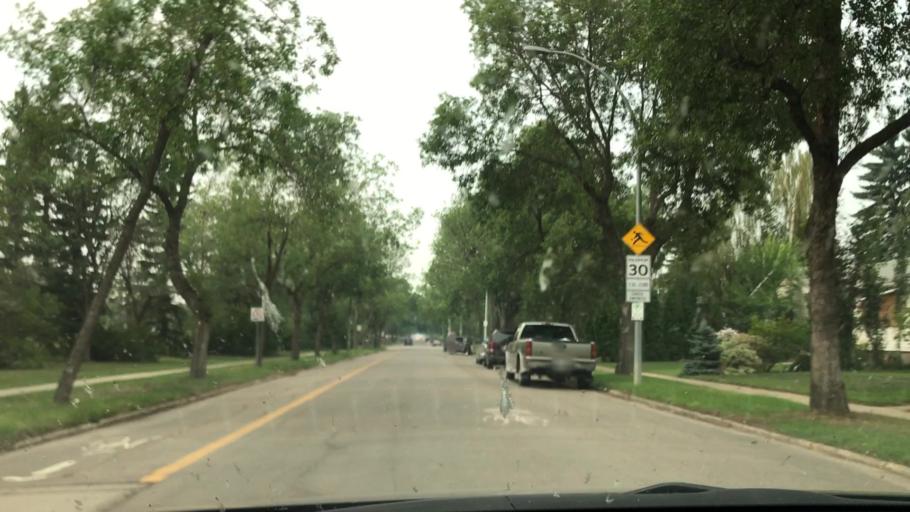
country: CA
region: Alberta
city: Edmonton
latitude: 53.5637
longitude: -113.5412
